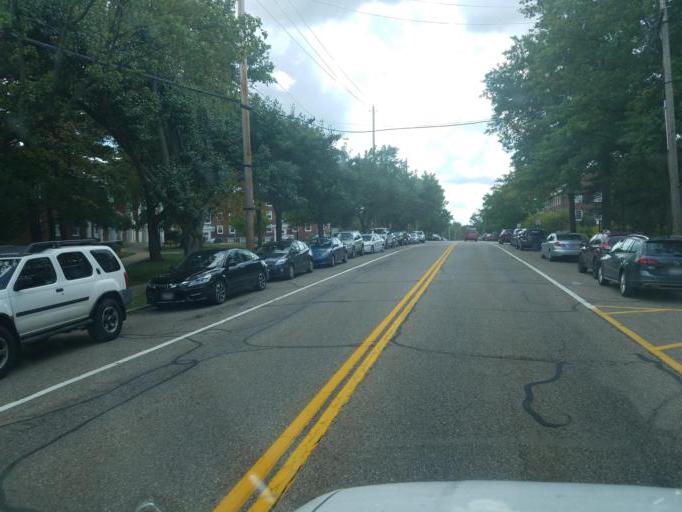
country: US
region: Ohio
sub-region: Portage County
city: Hiram
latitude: 41.3119
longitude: -81.1436
